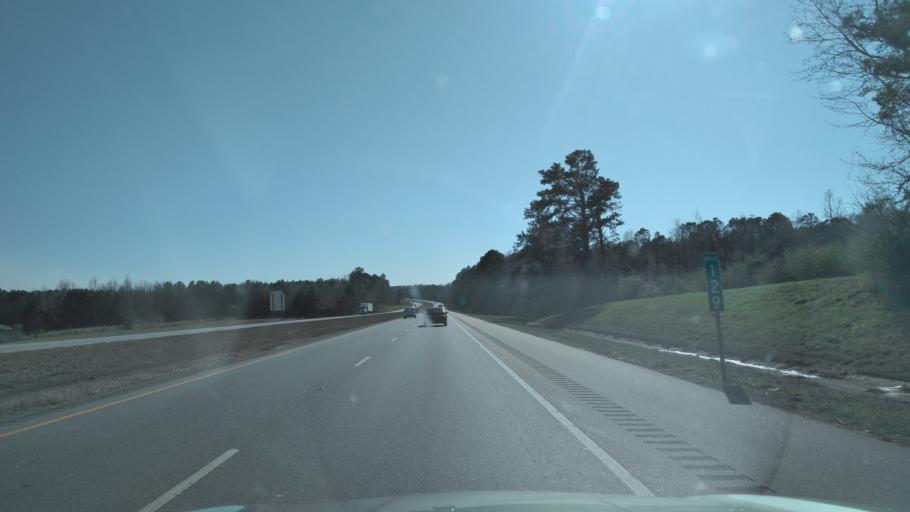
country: US
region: Alabama
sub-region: Butler County
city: Greenville
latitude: 31.8405
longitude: -86.6535
